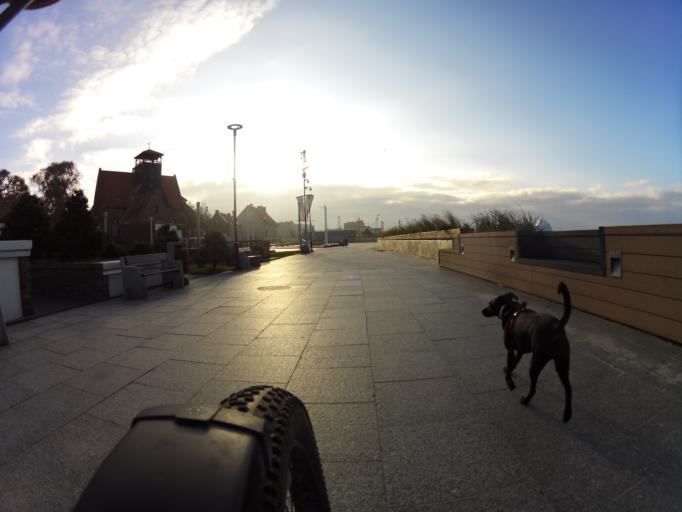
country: PL
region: Pomeranian Voivodeship
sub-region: Powiat pucki
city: Hel
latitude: 54.6056
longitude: 18.8010
